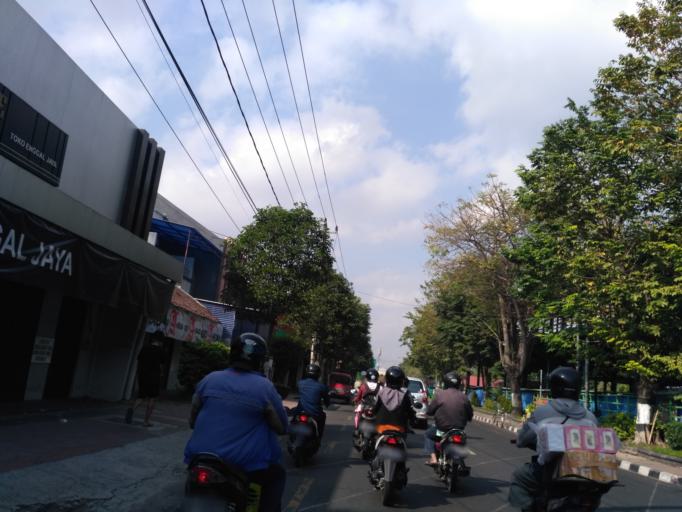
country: ID
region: Daerah Istimewa Yogyakarta
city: Yogyakarta
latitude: -7.8019
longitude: 110.3565
